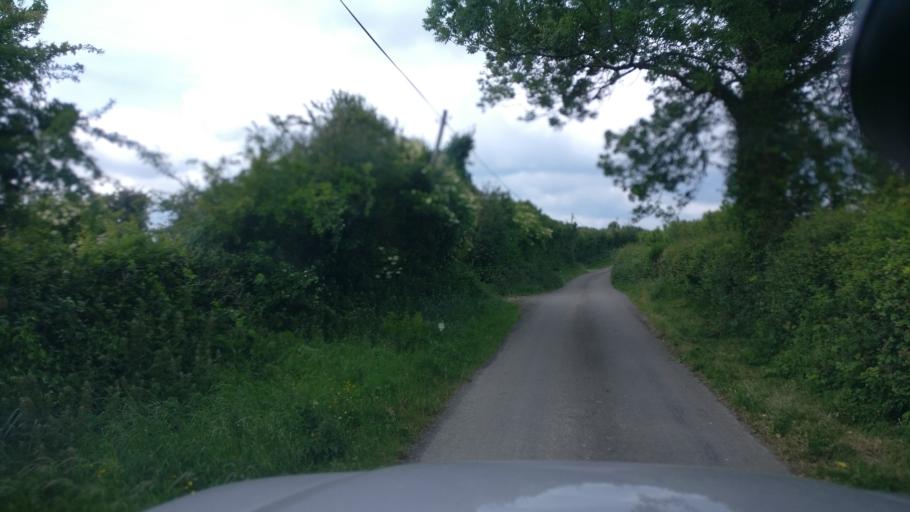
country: IE
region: Connaught
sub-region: County Galway
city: Ballinasloe
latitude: 53.2912
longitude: -8.3177
